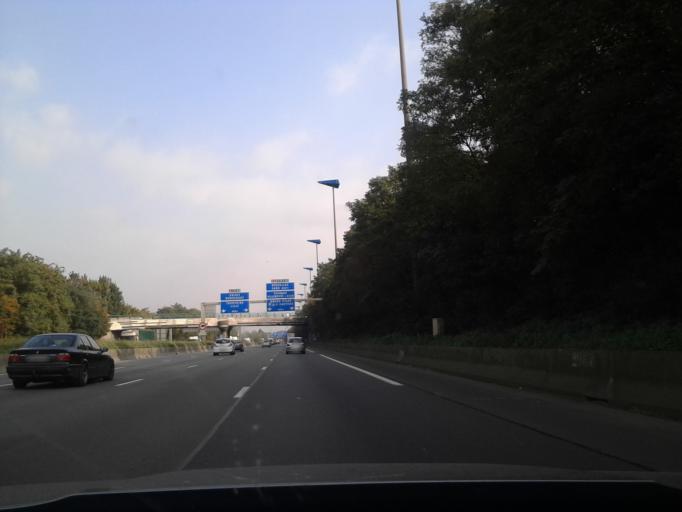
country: FR
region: Nord-Pas-de-Calais
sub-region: Departement du Nord
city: Ronchin
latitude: 50.5872
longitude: 3.0946
